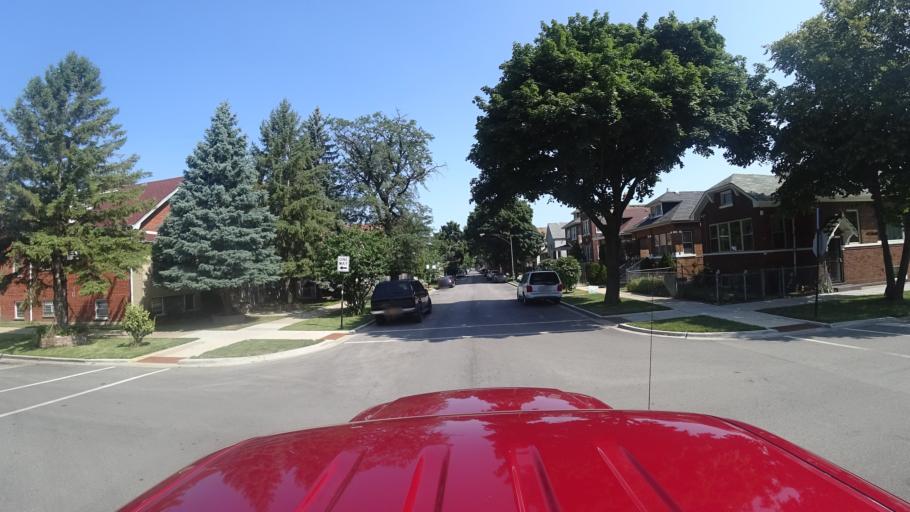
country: US
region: Illinois
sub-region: Cook County
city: Chicago
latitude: 41.7962
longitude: -87.6928
